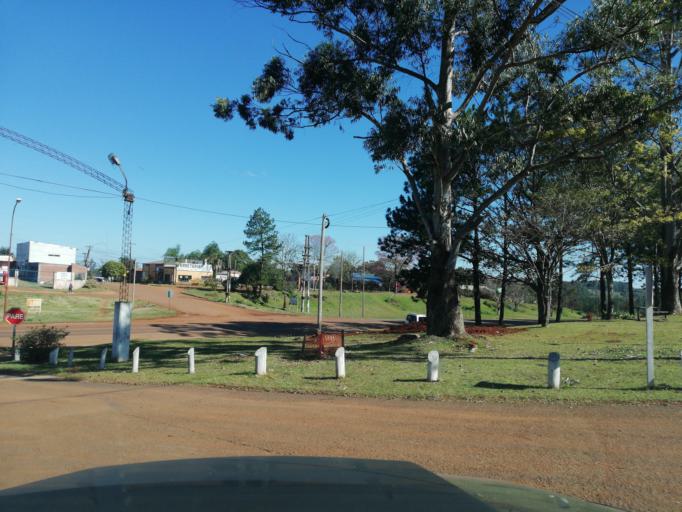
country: AR
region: Misiones
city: Aristobulo del Valle
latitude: -27.0846
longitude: -54.8377
